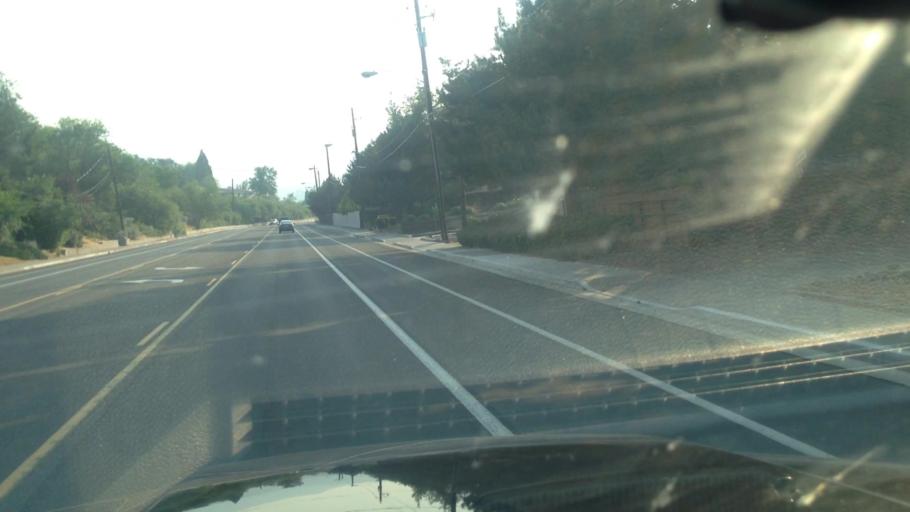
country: US
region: Nevada
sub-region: Washoe County
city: Reno
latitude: 39.5082
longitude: -119.8420
